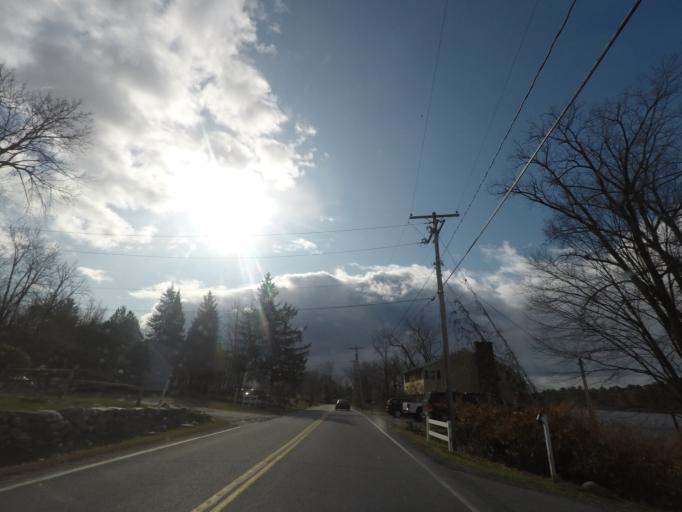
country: US
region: New York
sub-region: Saratoga County
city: Ballston Spa
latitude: 42.9509
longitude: -73.8495
